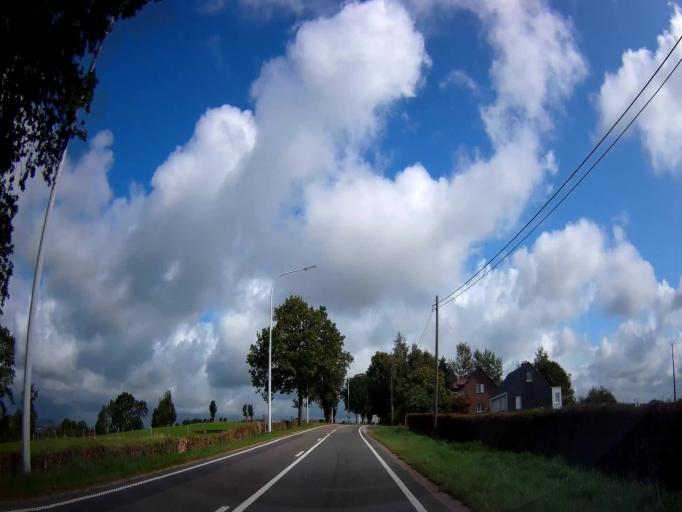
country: BE
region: Wallonia
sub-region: Province de Liege
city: Dison
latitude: 50.6537
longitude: 5.8852
